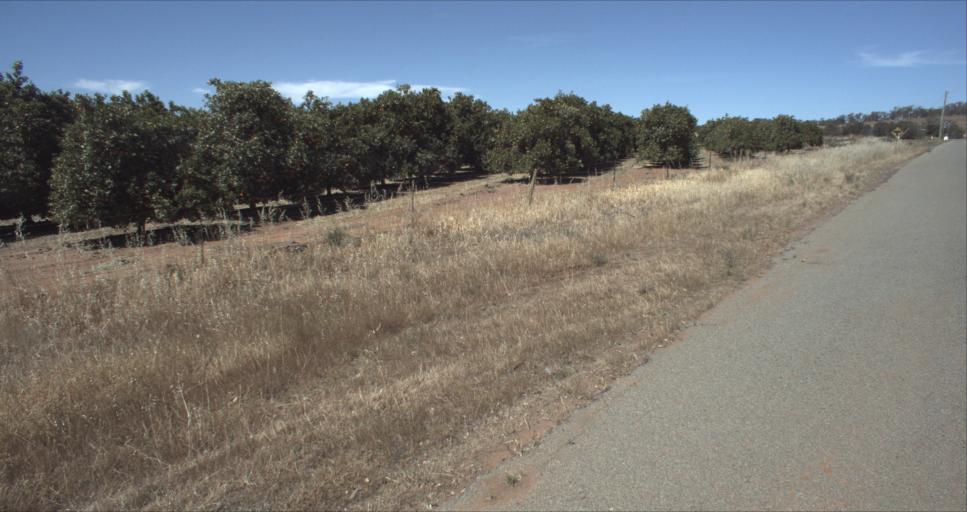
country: AU
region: New South Wales
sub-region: Leeton
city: Leeton
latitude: -34.6060
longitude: 146.4338
